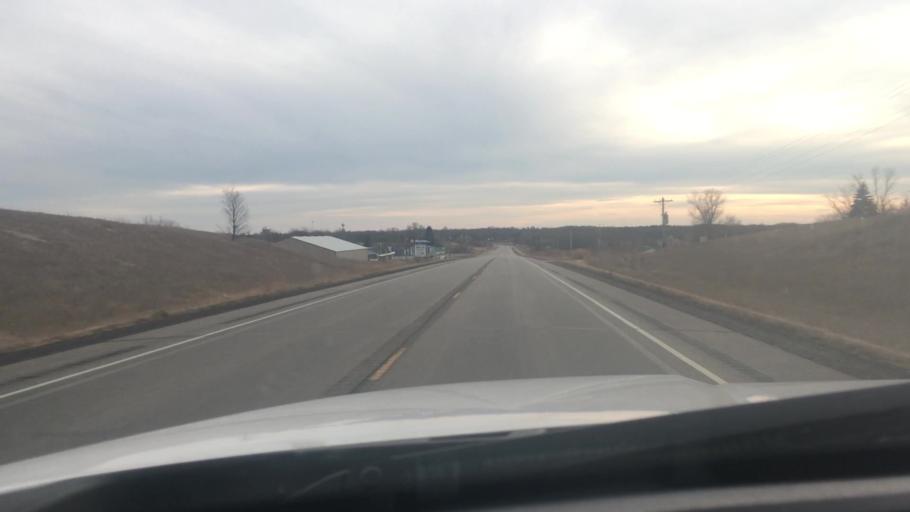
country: US
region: Minnesota
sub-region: Otter Tail County
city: Perham
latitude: 46.3050
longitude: -95.7183
